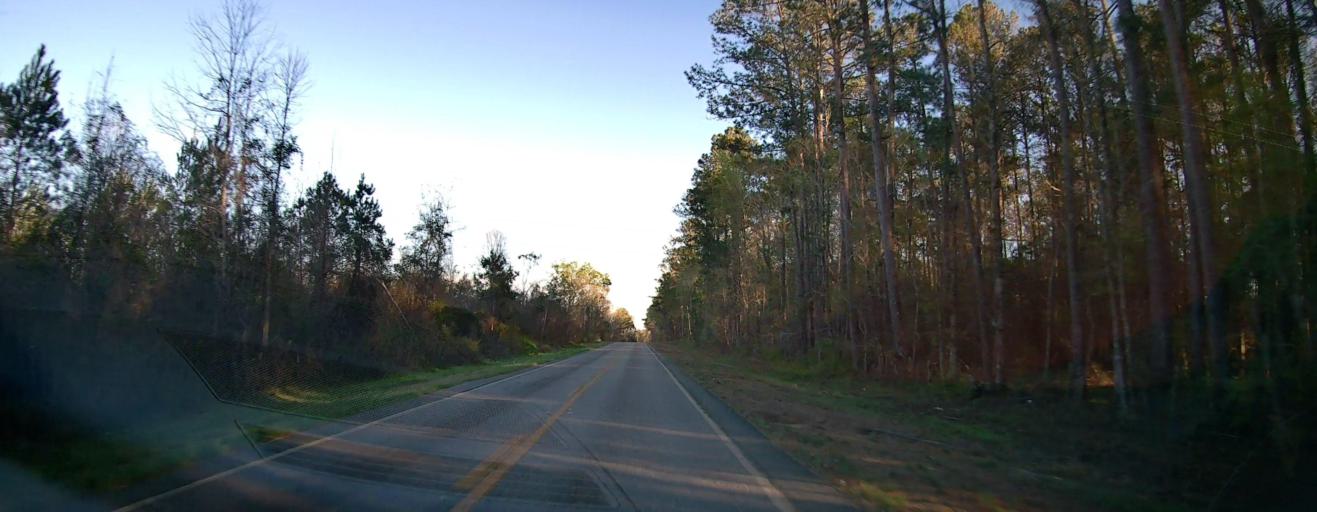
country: US
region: Georgia
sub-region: Wilcox County
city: Abbeville
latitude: 32.1073
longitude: -83.3124
